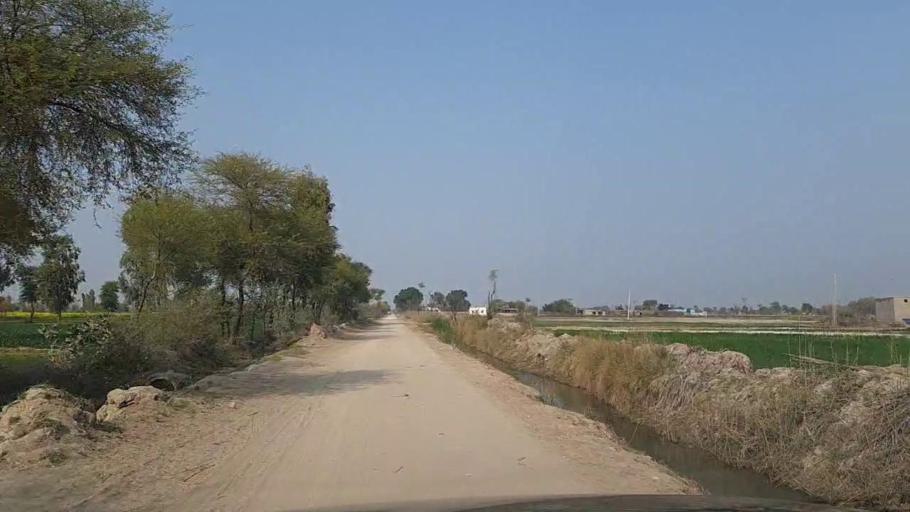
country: PK
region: Sindh
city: Daur
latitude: 26.3951
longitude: 68.4238
